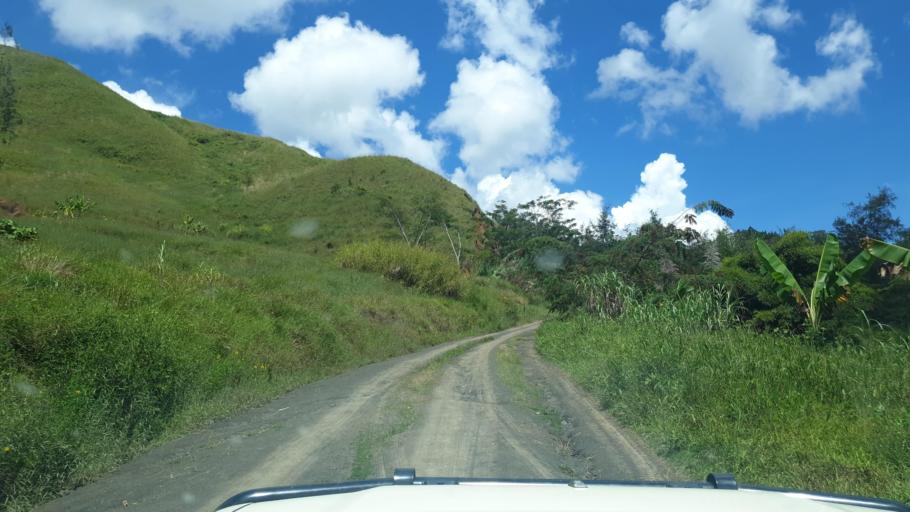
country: PG
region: Chimbu
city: Kundiawa
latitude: -6.2565
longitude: 145.1381
